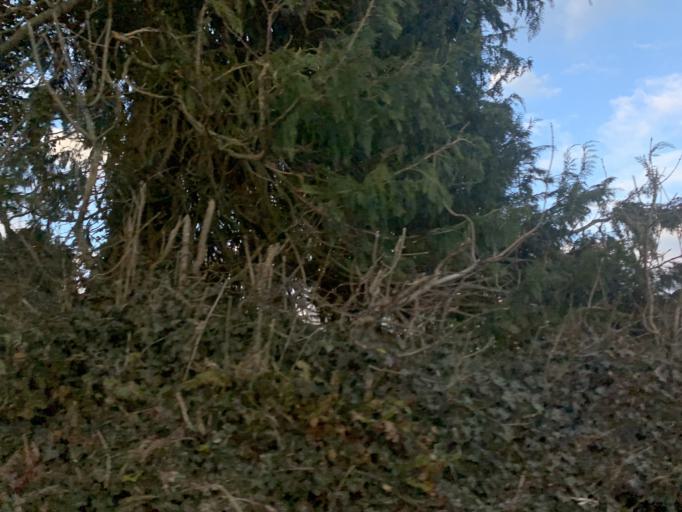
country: IE
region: Connaught
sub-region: Maigh Eo
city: Ballyhaunis
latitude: 53.8603
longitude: -8.7449
